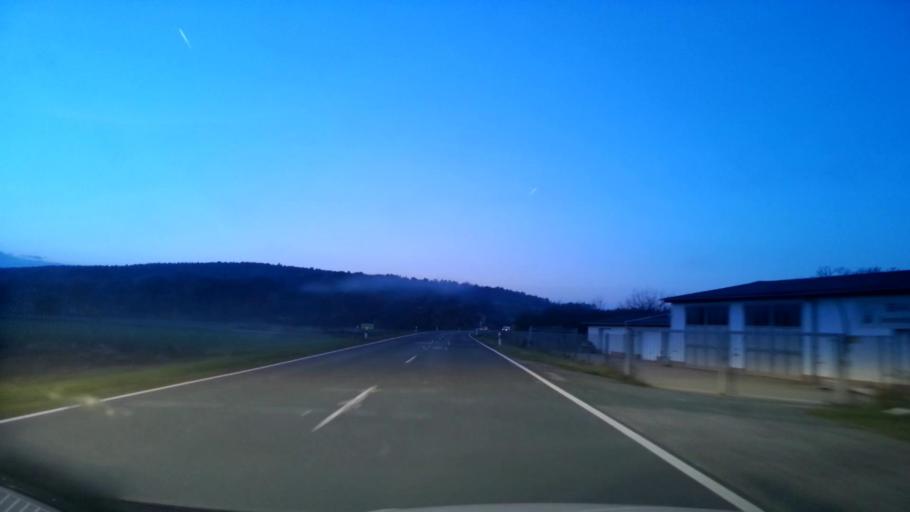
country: DE
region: Bavaria
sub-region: Upper Franconia
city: Pettstadt
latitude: 49.8357
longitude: 10.9327
